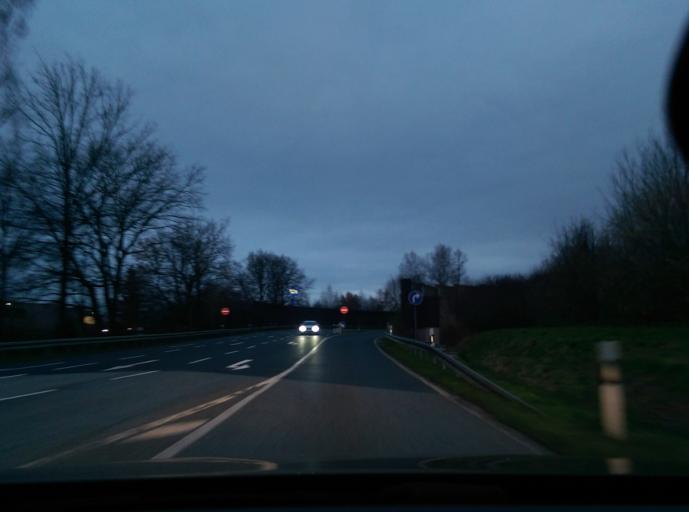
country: DE
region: Lower Saxony
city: Isernhagen Farster Bauerschaft
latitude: 52.4903
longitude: 9.8395
